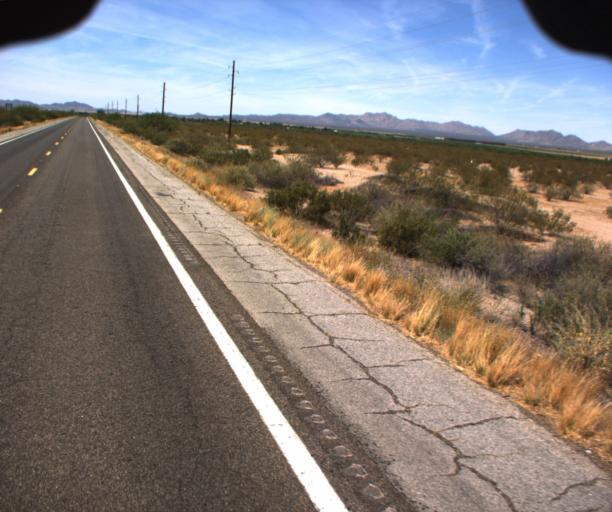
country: US
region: Arizona
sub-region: La Paz County
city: Salome
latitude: 33.8277
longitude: -113.5159
